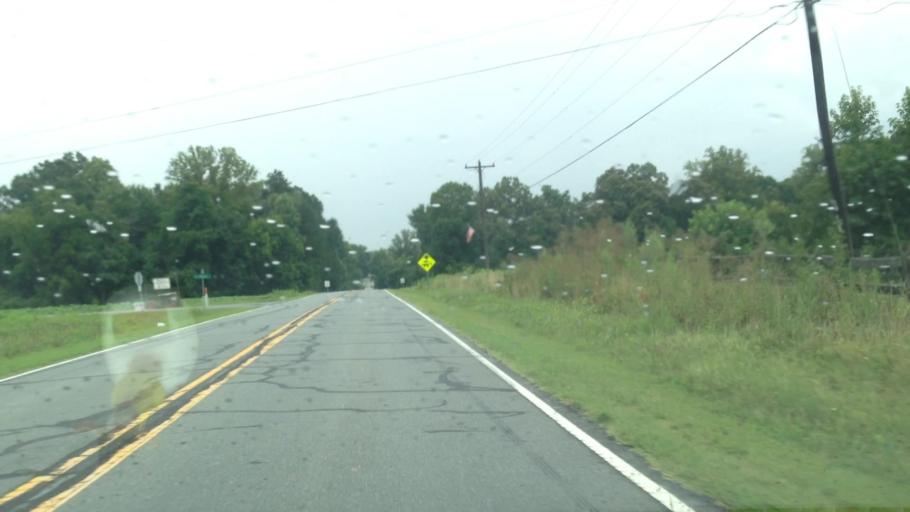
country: US
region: North Carolina
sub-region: Stokes County
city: Walnut Cove
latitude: 36.3370
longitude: -80.0502
